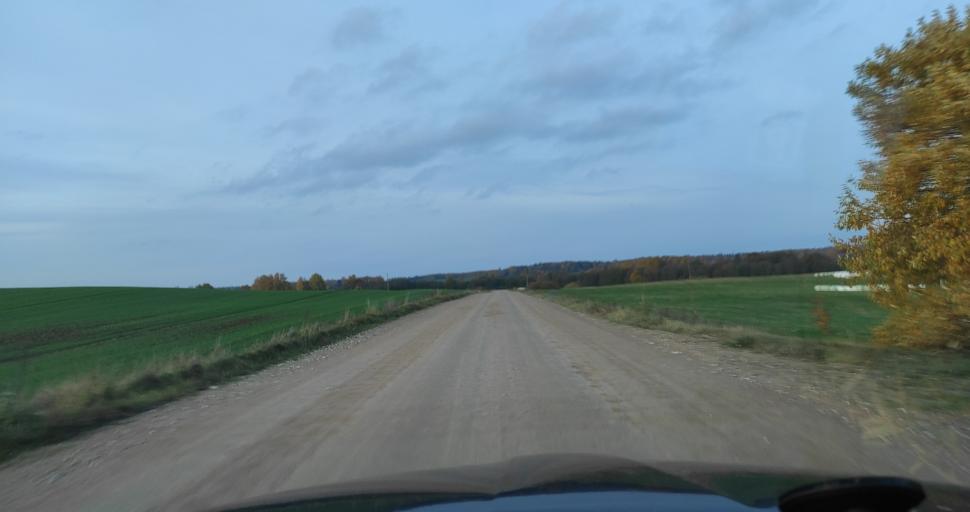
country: LV
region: Aizpute
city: Aizpute
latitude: 56.6867
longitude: 21.7914
